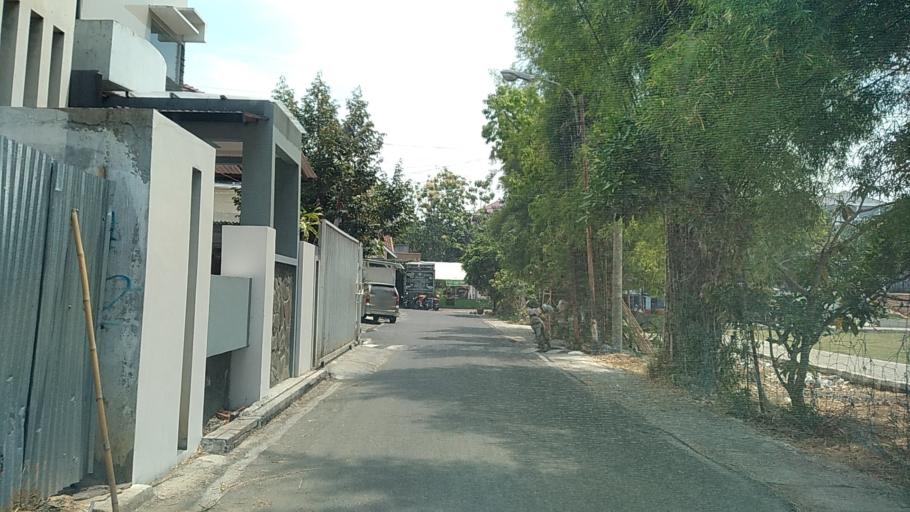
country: ID
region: Central Java
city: Semarang
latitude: -7.0514
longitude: 110.4285
